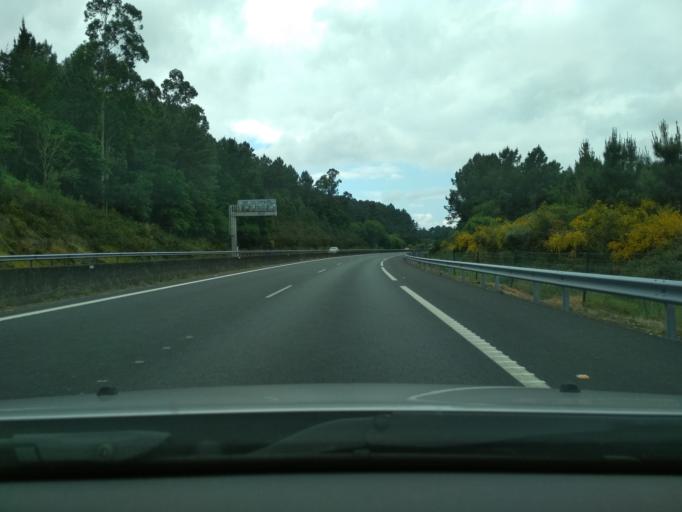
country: ES
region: Galicia
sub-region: Provincia da Coruna
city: Padron
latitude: 42.7931
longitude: -8.6388
